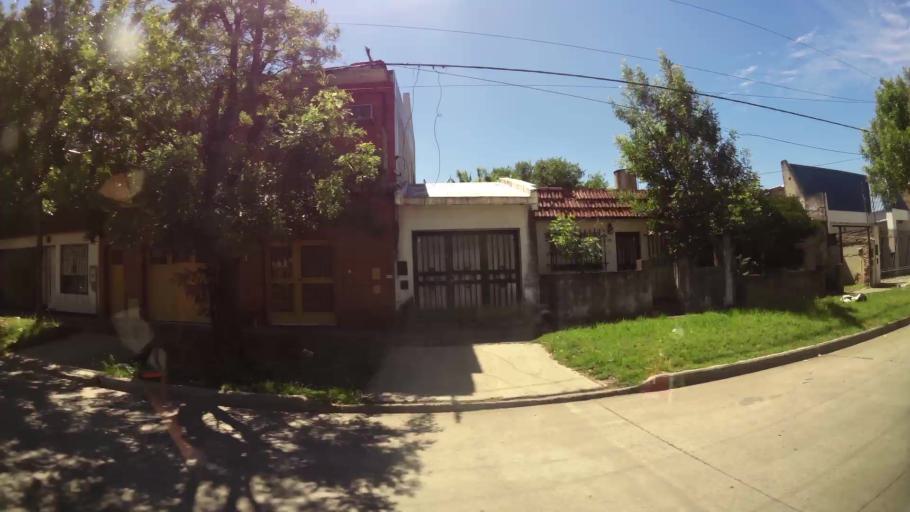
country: AR
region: Santa Fe
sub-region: Departamento de Rosario
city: Rosario
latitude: -32.9640
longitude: -60.7012
